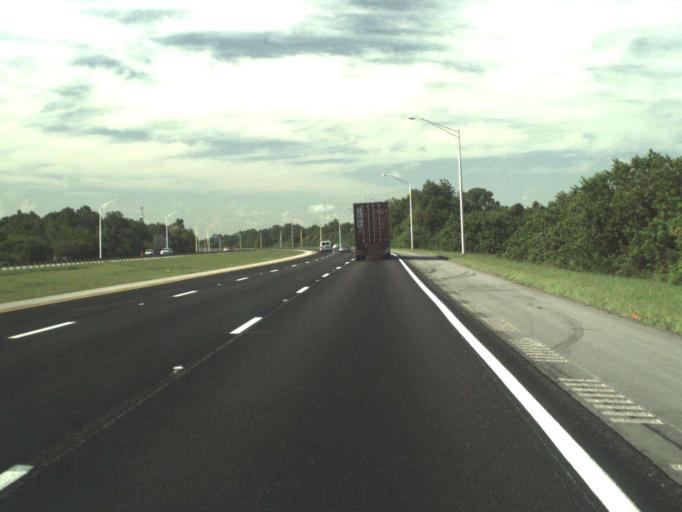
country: US
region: Florida
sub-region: Indian River County
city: West Vero Corridor
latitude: 27.6228
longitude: -80.5159
